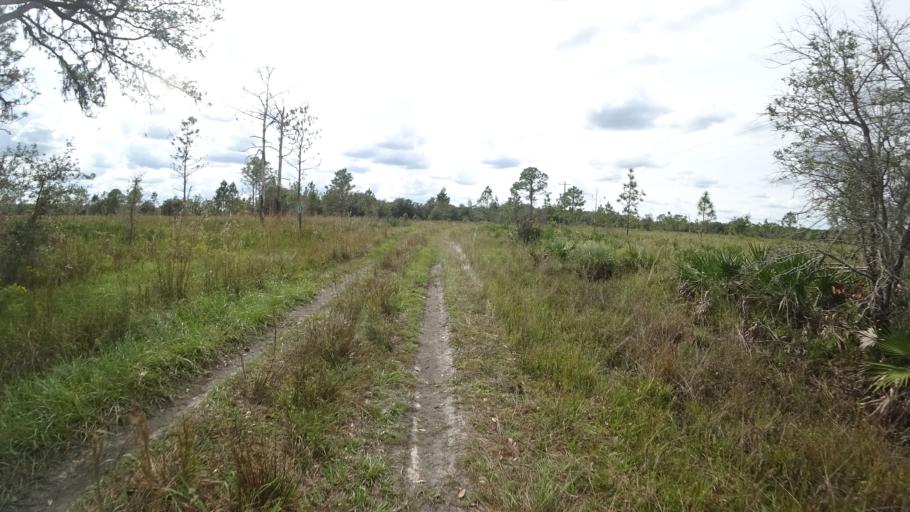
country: US
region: Florida
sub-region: Hillsborough County
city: Wimauma
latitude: 27.5370
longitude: -82.1460
